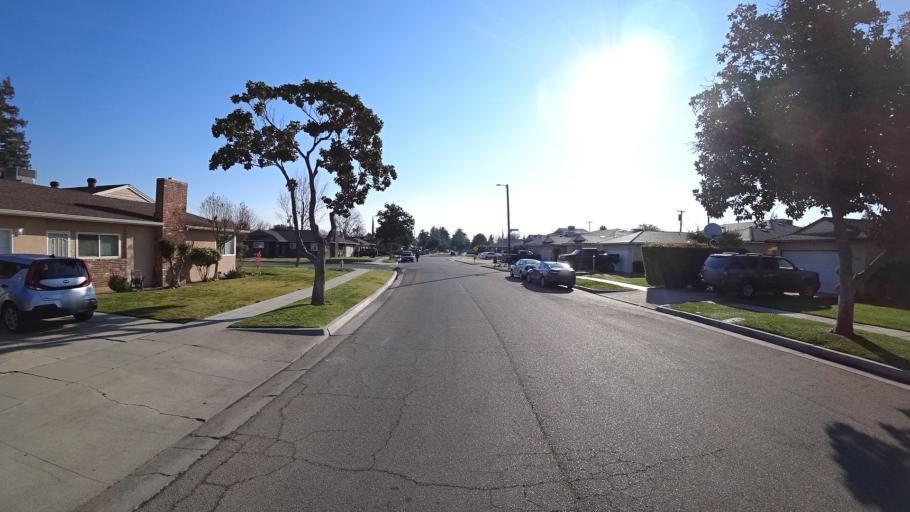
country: US
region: California
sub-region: Fresno County
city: Fresno
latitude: 36.8201
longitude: -119.7766
